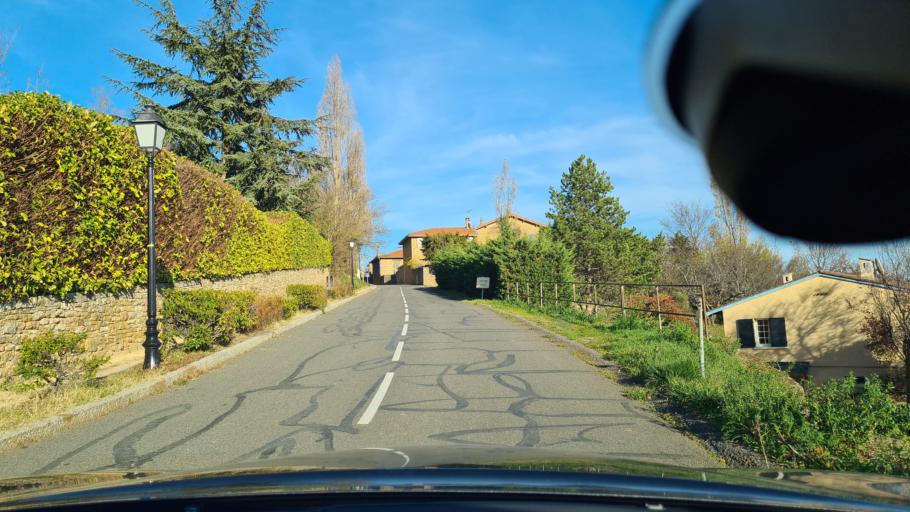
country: FR
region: Rhone-Alpes
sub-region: Departement du Rhone
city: Chasselay
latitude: 45.8593
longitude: 4.7972
